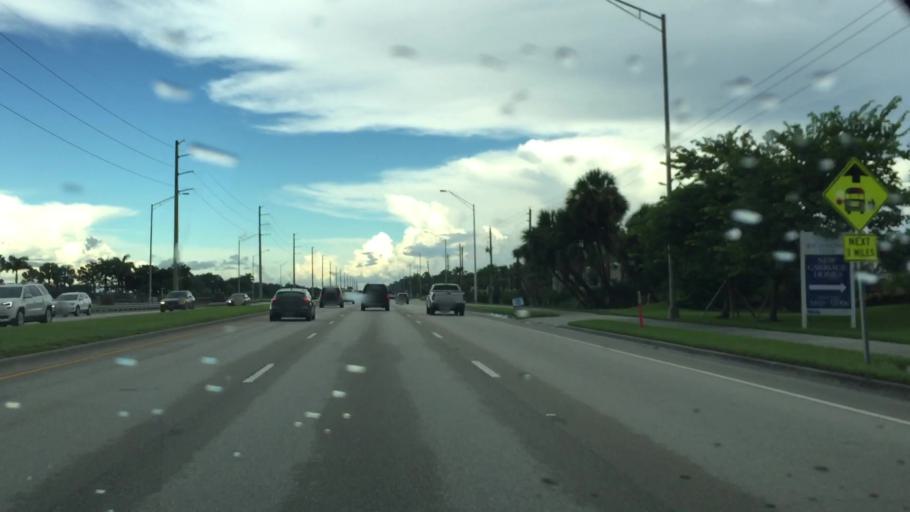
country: US
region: Florida
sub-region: Collier County
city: Vineyards
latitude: 26.2730
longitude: -81.6753
